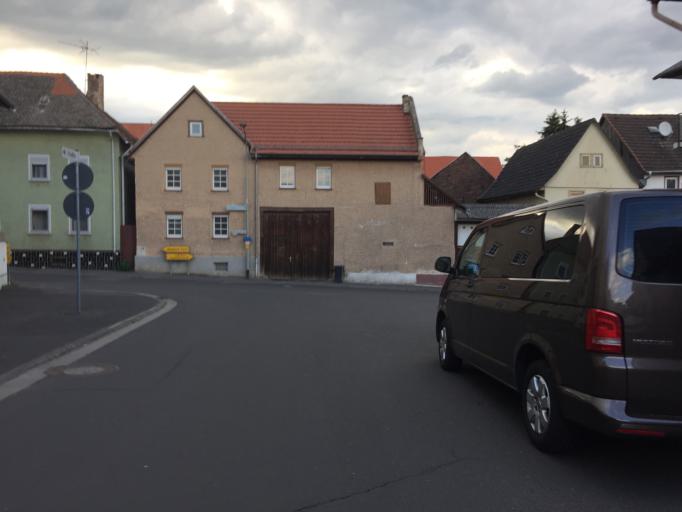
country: DE
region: Hesse
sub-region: Regierungsbezirk Darmstadt
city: Rockenberg
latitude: 50.4395
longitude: 8.7060
